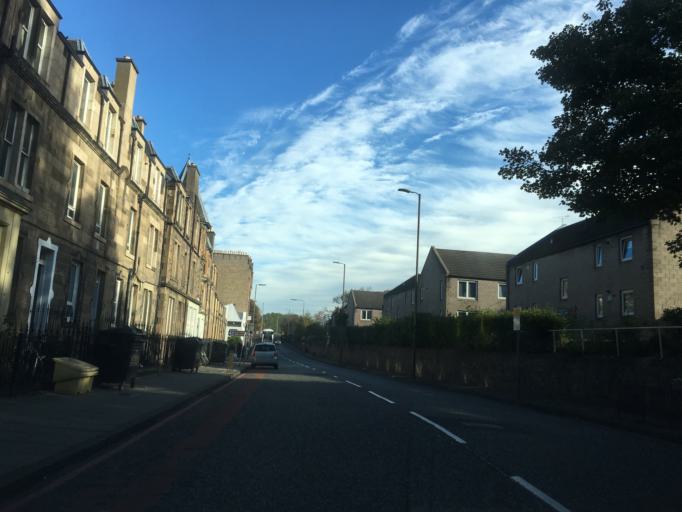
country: GB
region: Scotland
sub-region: Edinburgh
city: Edinburgh
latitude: 55.9378
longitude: -3.2253
